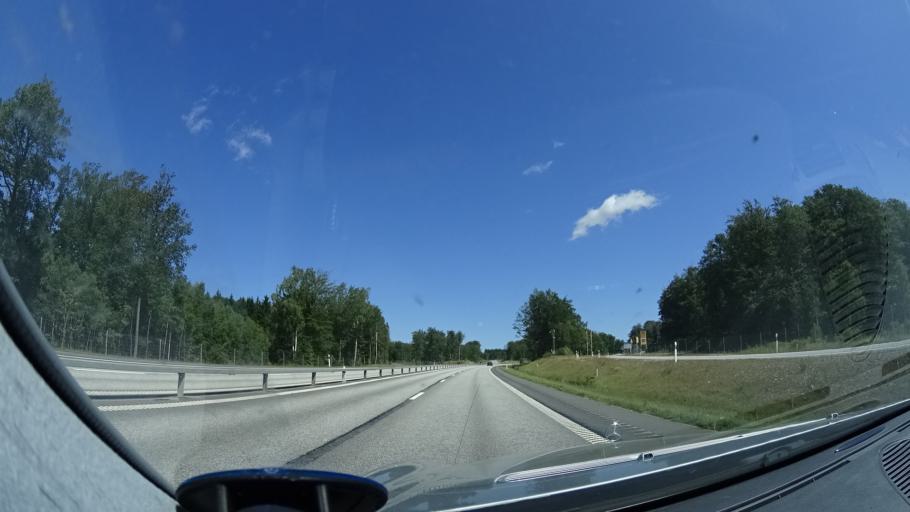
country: SE
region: Skane
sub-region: Horby Kommun
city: Hoerby
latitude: 55.8998
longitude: 13.7264
